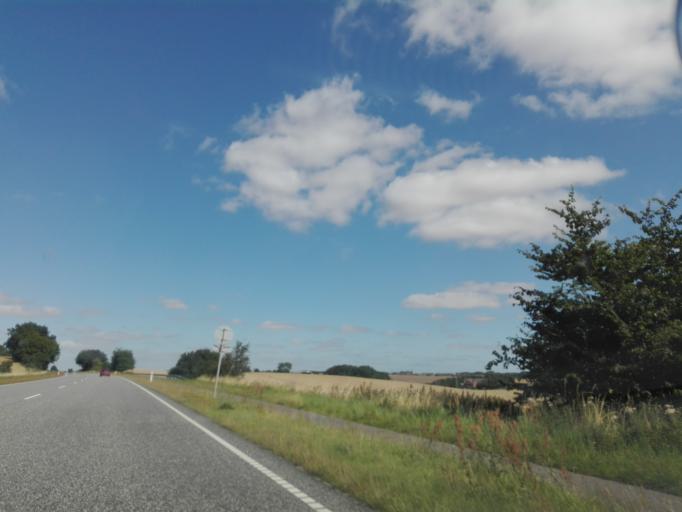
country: DK
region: Central Jutland
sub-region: Favrskov Kommune
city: Hadsten
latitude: 56.3911
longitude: 10.0854
